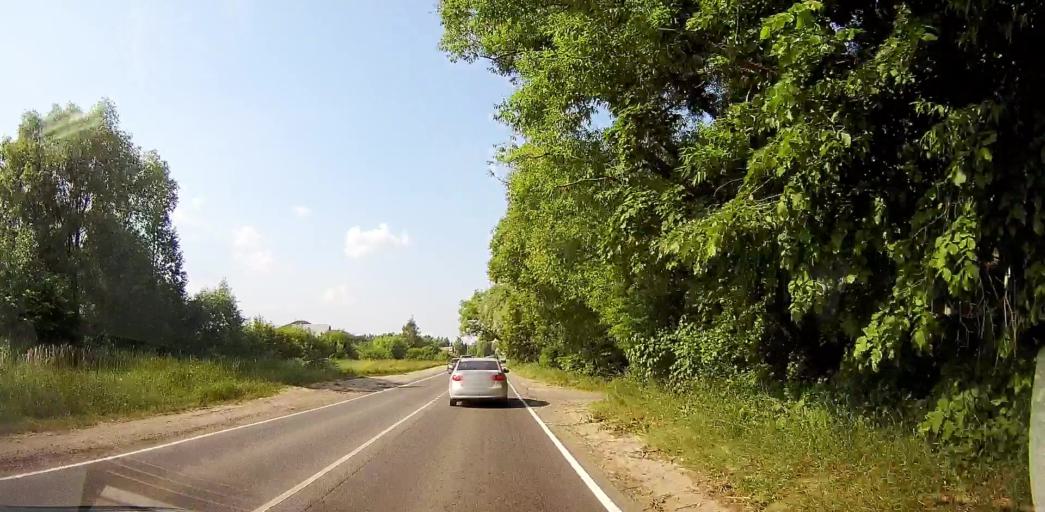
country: RU
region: Moskovskaya
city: Zhitnevo
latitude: 55.3143
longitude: 37.9001
